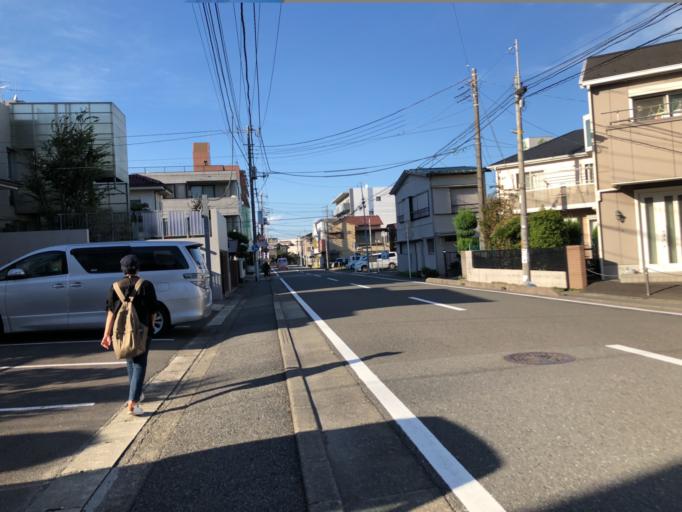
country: JP
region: Tokyo
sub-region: Machida-shi
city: Machida
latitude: 35.5708
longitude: 139.3958
